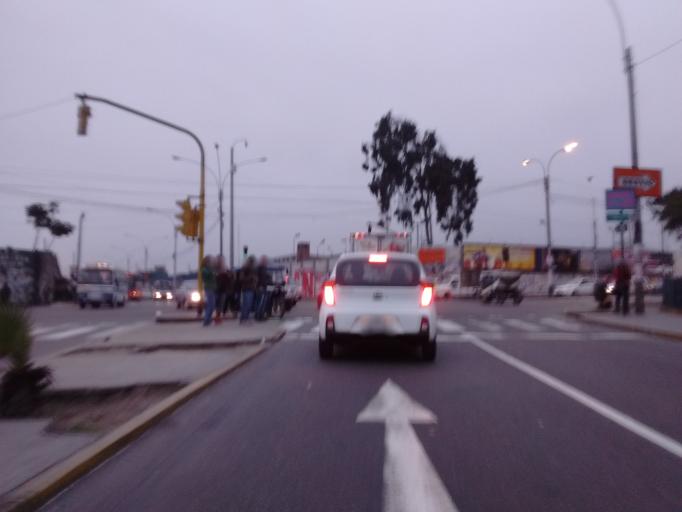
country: PE
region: Callao
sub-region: Callao
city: Callao
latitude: -12.0468
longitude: -77.0768
